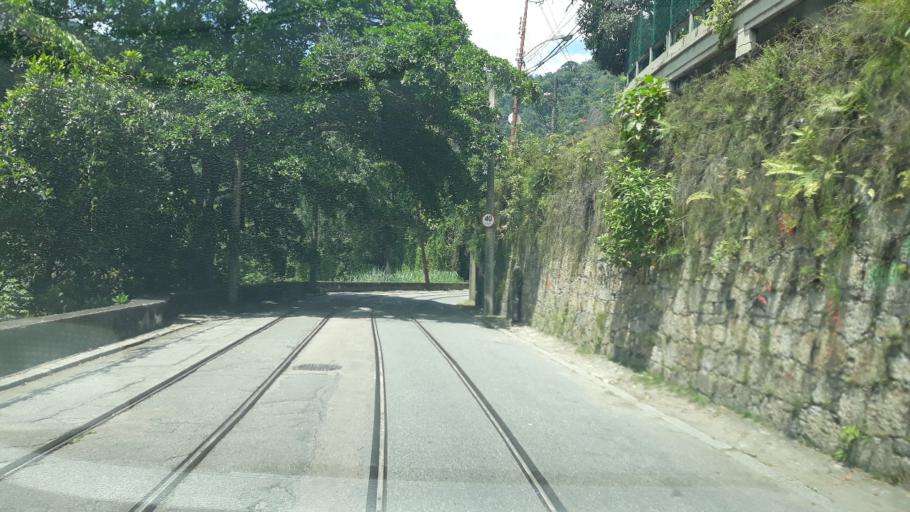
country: BR
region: Rio de Janeiro
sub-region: Rio De Janeiro
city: Rio de Janeiro
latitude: -22.9381
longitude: -43.2066
